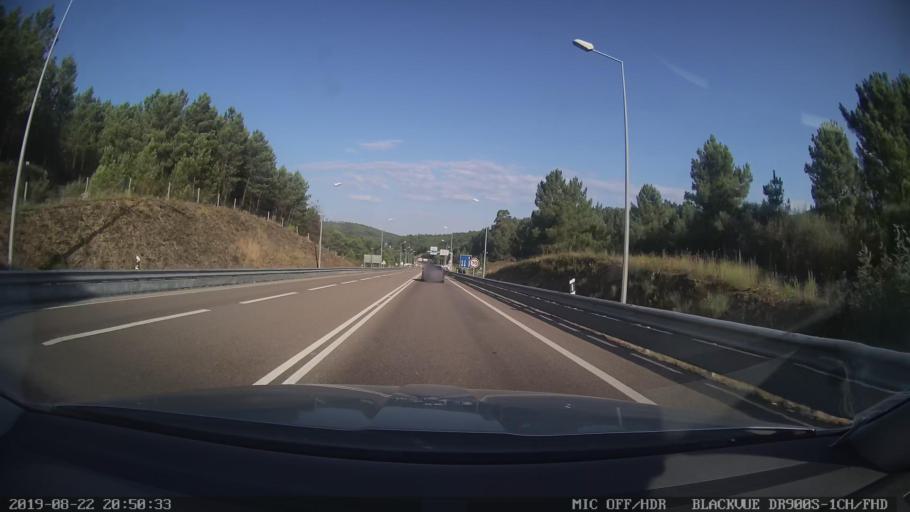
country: PT
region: Castelo Branco
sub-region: Proenca-A-Nova
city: Proenca-a-Nova
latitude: 39.7559
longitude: -7.9413
